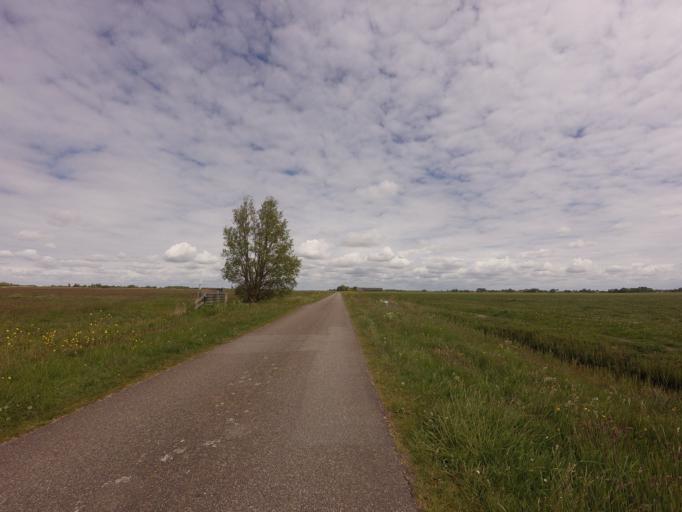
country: NL
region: Friesland
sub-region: Sudwest Fryslan
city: Koudum
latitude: 52.9099
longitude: 5.5037
